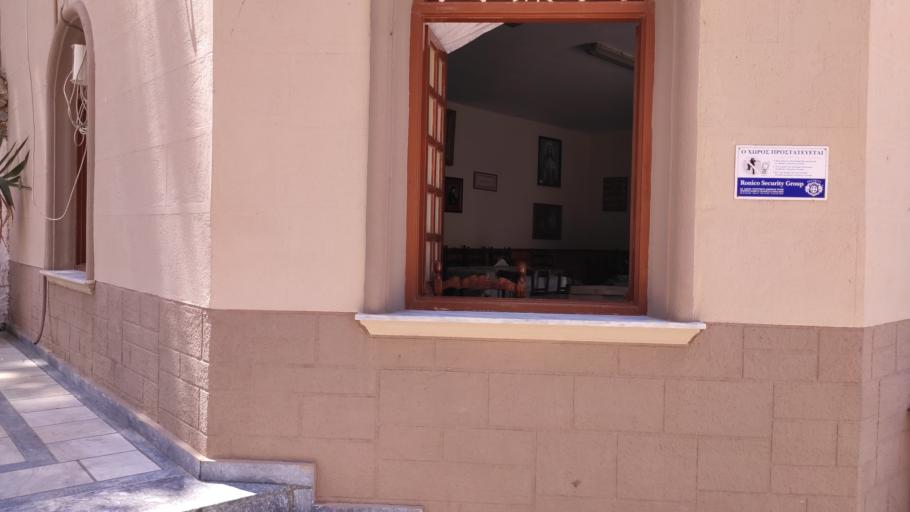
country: GR
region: South Aegean
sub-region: Nomos Dodekanisou
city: Kalymnos
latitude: 36.9462
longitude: 26.9843
